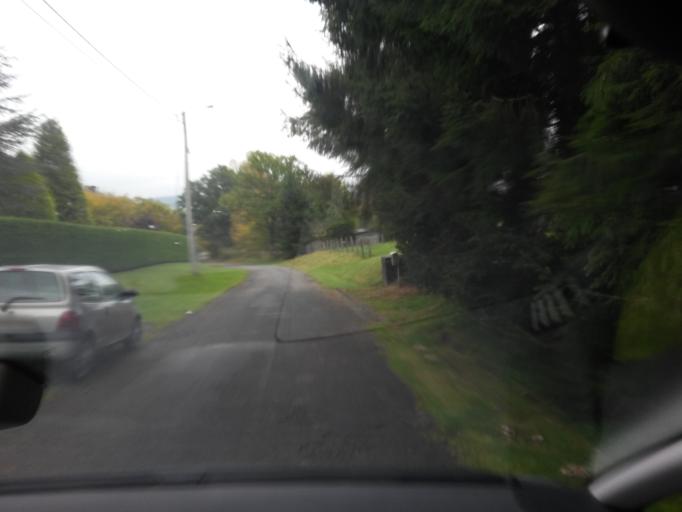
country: BE
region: Wallonia
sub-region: Province du Luxembourg
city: Chiny
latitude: 49.7643
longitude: 5.3899
